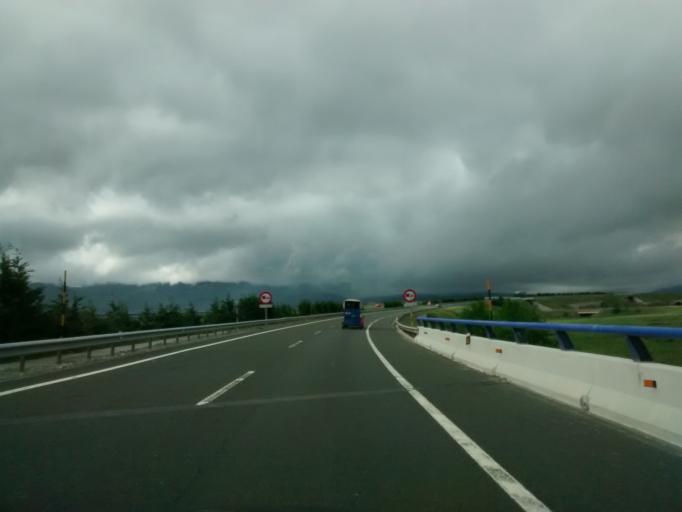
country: ES
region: Cantabria
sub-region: Provincia de Cantabria
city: Villaescusa
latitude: 42.9707
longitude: -4.1565
